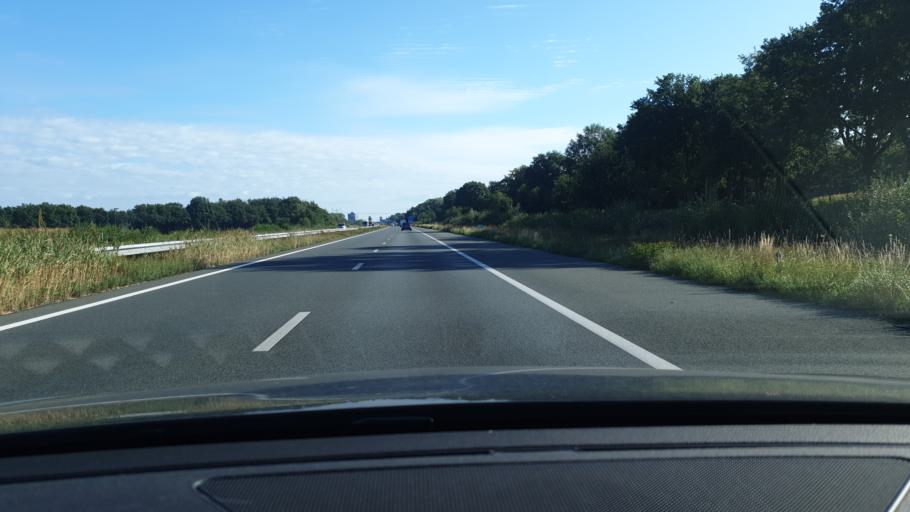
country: NL
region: North Brabant
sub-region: Gemeente Veghel
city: Eerde
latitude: 51.5852
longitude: 5.4959
